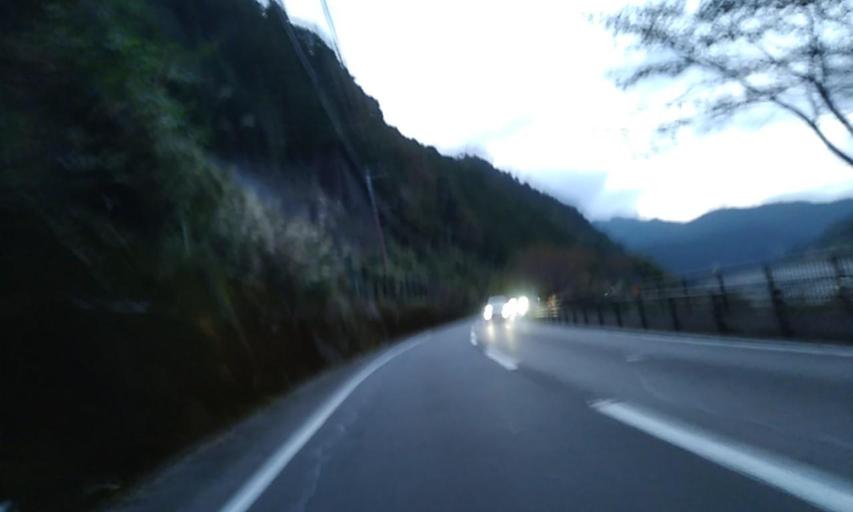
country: JP
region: Wakayama
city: Shingu
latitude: 33.7269
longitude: 135.9529
